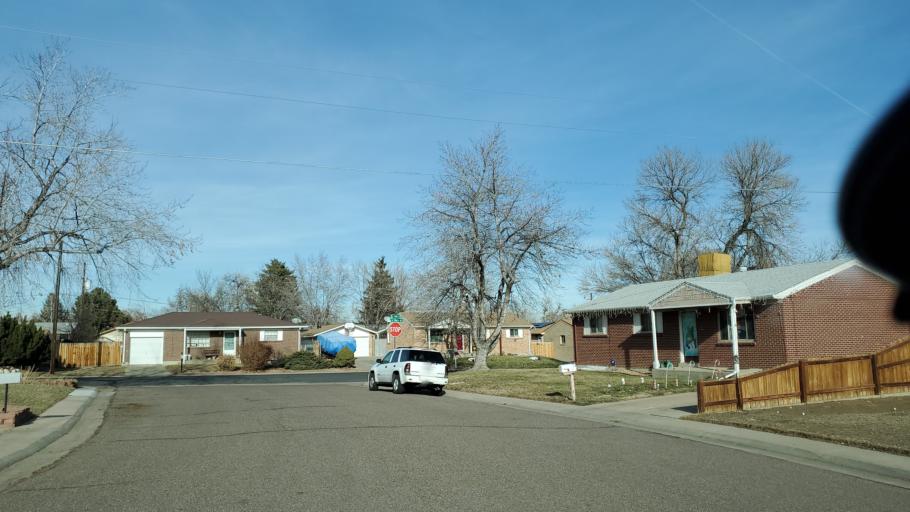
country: US
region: Colorado
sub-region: Adams County
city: Northglenn
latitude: 39.9073
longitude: -104.9613
